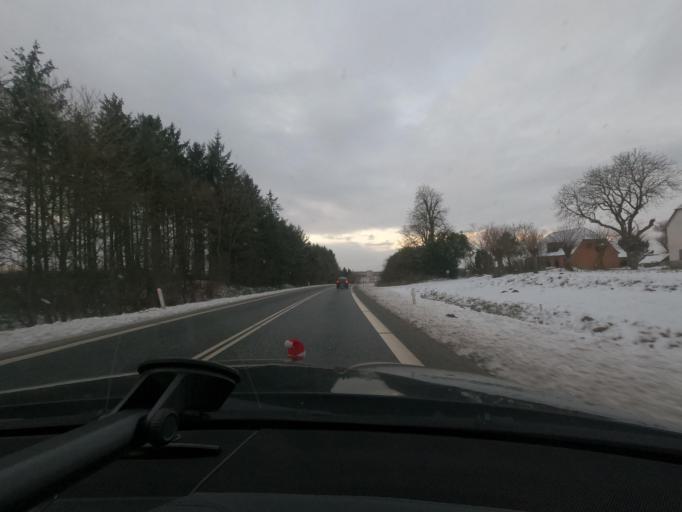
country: DK
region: South Denmark
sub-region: Aabenraa Kommune
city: Krusa
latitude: 54.8610
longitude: 9.4462
